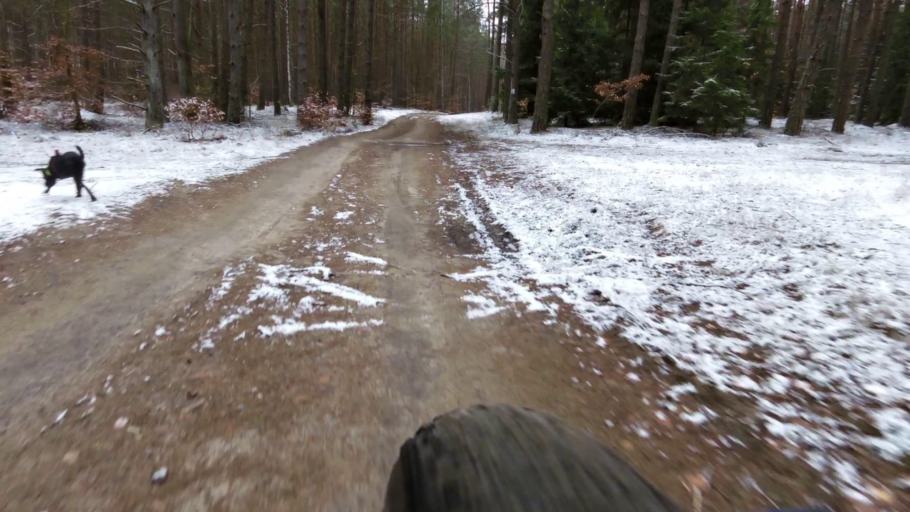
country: PL
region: West Pomeranian Voivodeship
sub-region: Powiat walecki
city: Miroslawiec
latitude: 53.3078
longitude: 16.0674
